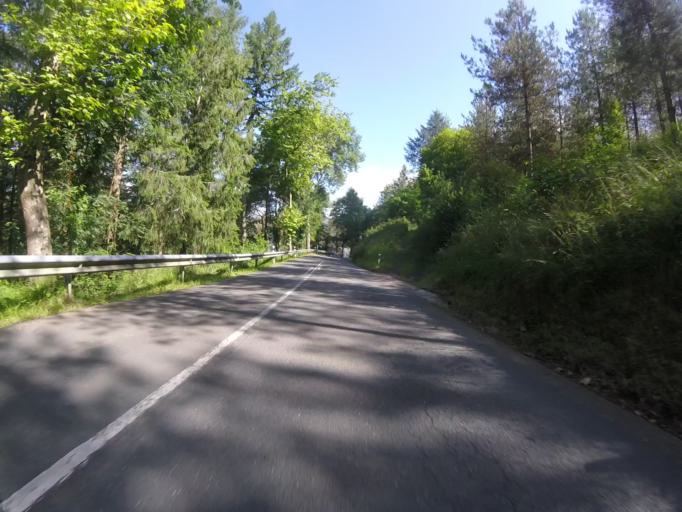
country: ES
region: Basque Country
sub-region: Provincia de Guipuzcoa
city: Ormaiztegui
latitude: 43.0942
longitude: -2.2400
